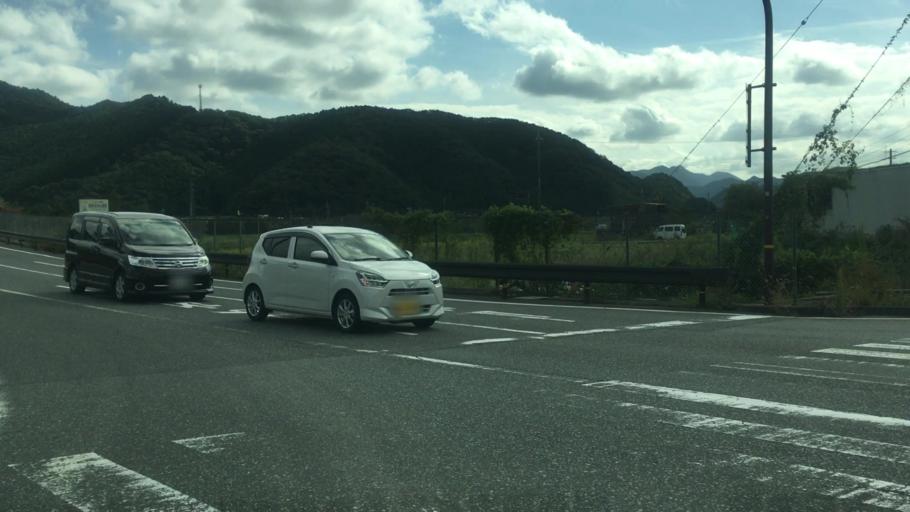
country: JP
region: Kyoto
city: Fukuchiyama
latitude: 35.2430
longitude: 135.0082
